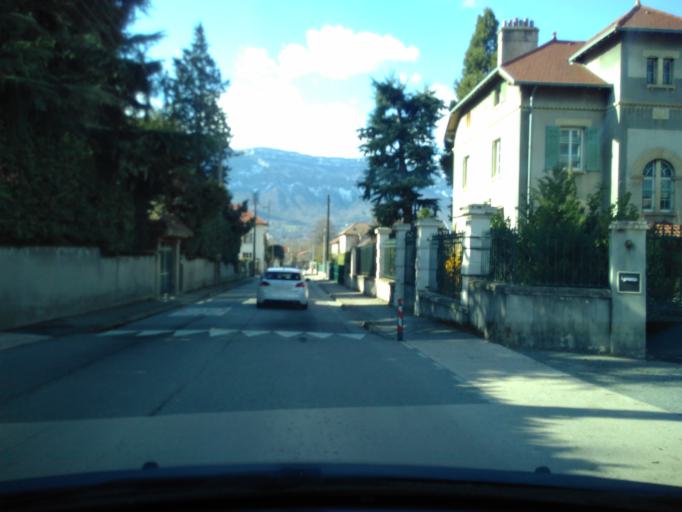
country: FR
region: Rhone-Alpes
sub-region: Departement de l'Isere
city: Domene
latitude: 45.2038
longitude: 5.8369
